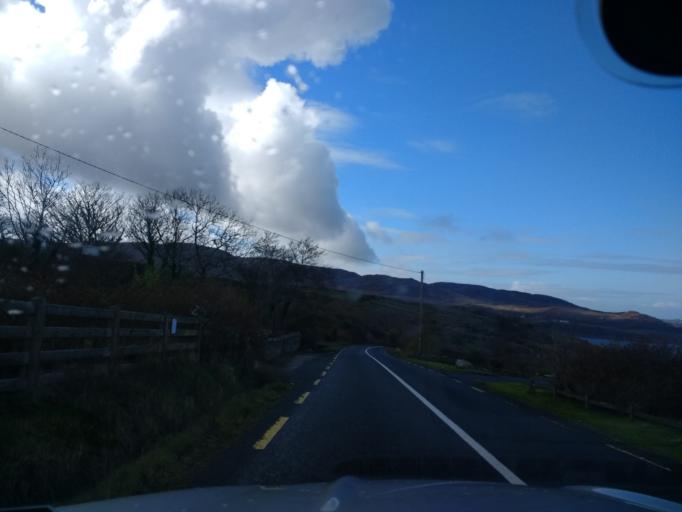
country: IE
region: Ulster
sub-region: County Donegal
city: Buncrana
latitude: 55.1554
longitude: -7.5591
